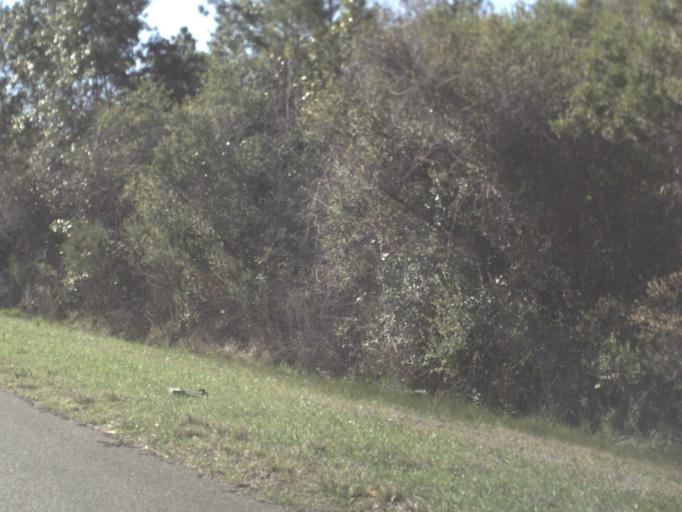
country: US
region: Florida
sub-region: Calhoun County
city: Blountstown
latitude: 30.4294
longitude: -85.1070
